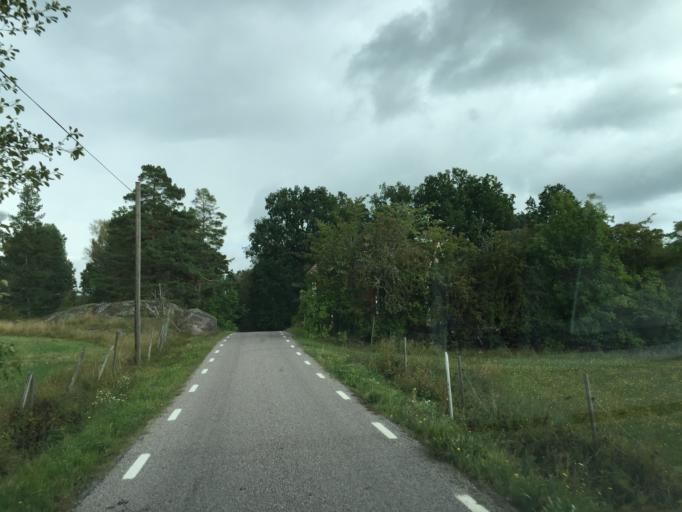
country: SE
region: Kalmar
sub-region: Vasterviks Kommun
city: Gamleby
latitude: 57.7875
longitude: 16.4283
